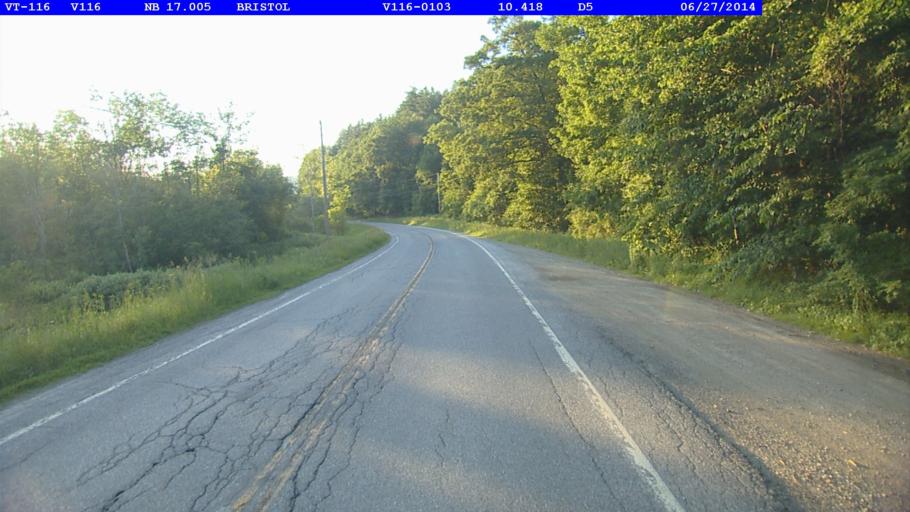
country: US
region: Vermont
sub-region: Addison County
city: Bristol
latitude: 44.1602
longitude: -73.0496
